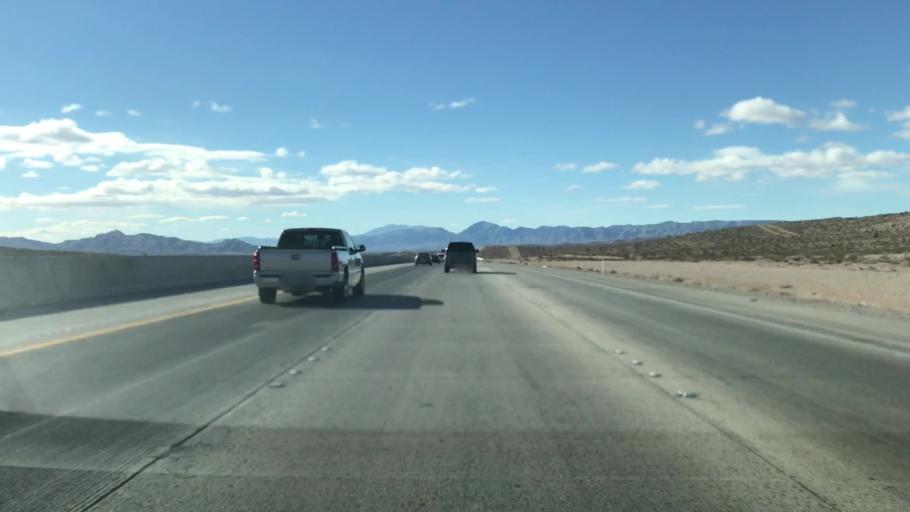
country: US
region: Nevada
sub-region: Clark County
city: Enterprise
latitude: 35.8711
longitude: -115.2425
